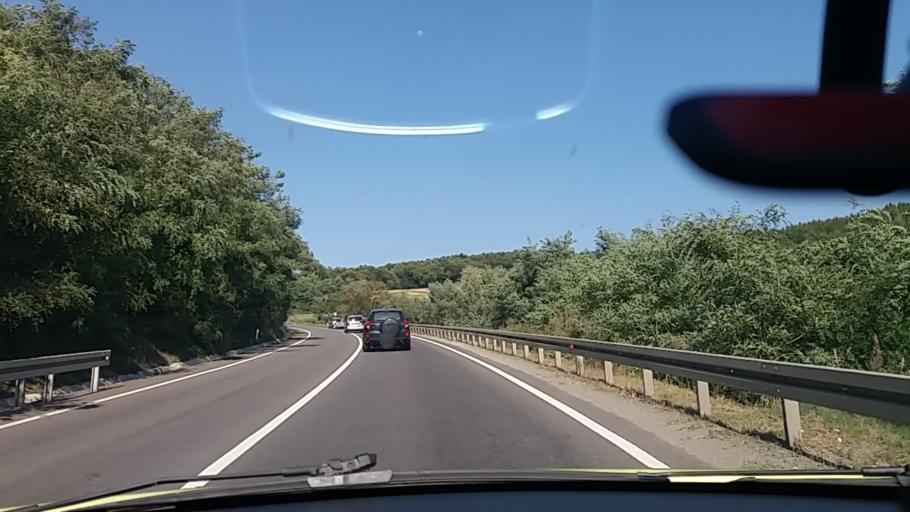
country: RO
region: Sibiu
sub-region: Comuna Slimnic
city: Slimnic
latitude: 45.9346
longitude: 24.1713
